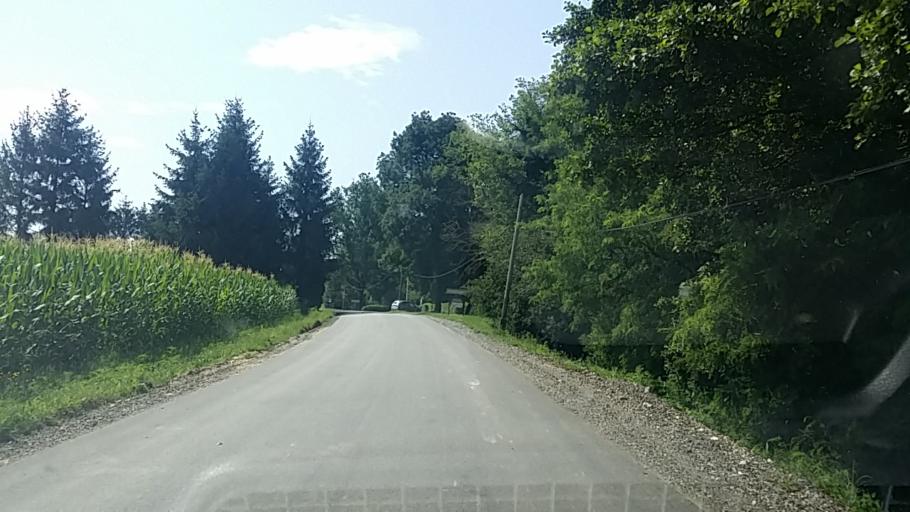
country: HR
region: Medimurska
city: Podturen
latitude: 46.5041
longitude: 16.5764
